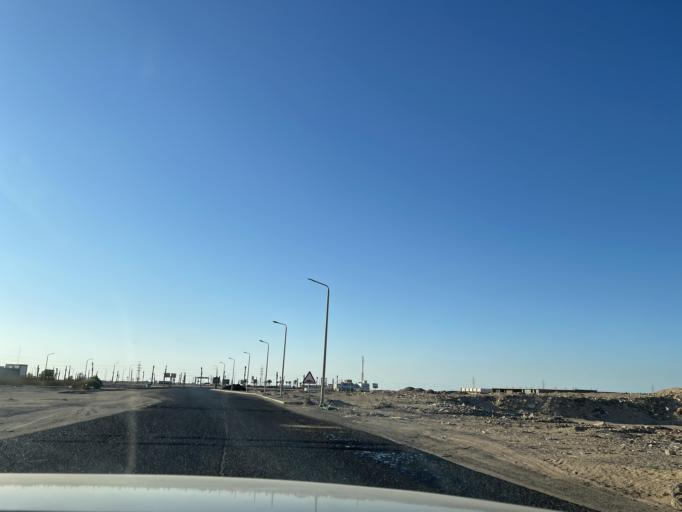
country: EG
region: Red Sea
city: Hurghada
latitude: 27.2281
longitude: 33.7820
